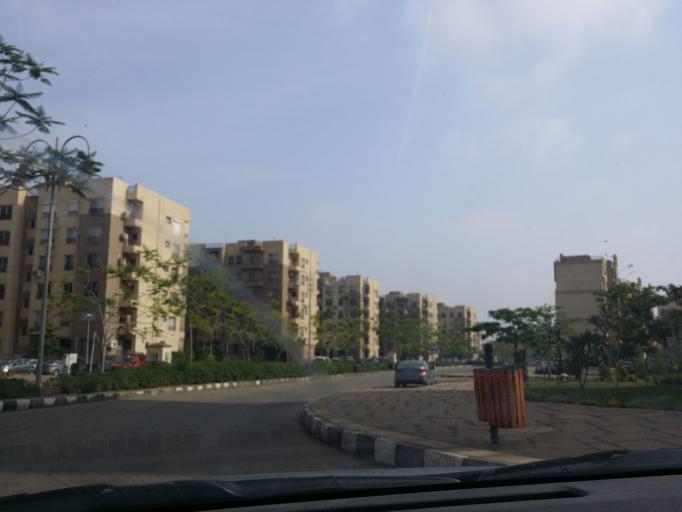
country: EG
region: Muhafazat al Qalyubiyah
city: Al Khankah
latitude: 30.0819
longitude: 31.6451
